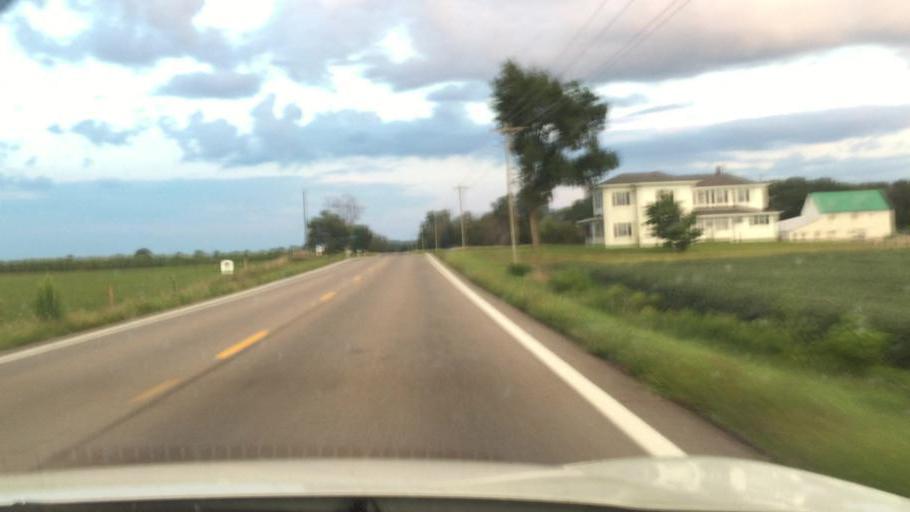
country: US
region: Ohio
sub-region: Champaign County
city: Mechanicsburg
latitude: 40.0530
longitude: -83.5274
